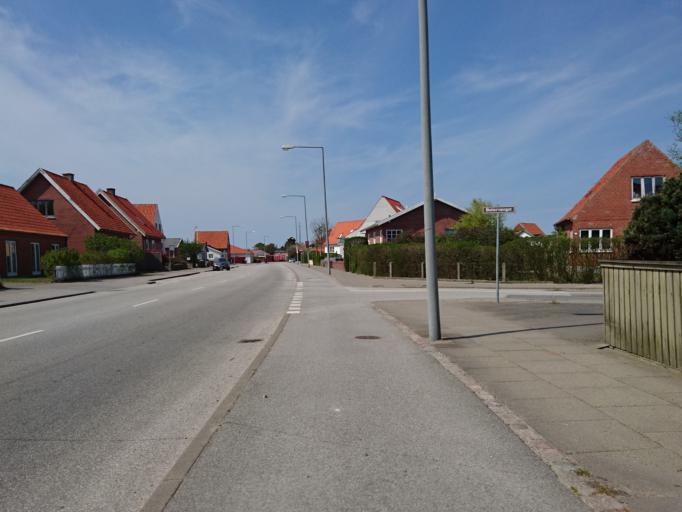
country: DK
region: North Denmark
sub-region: Frederikshavn Kommune
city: Skagen
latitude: 57.7226
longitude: 10.5743
